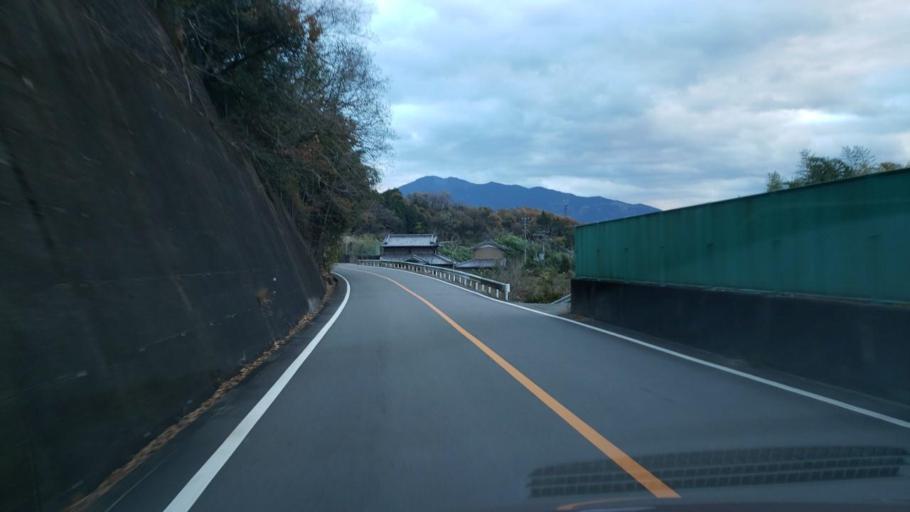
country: JP
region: Tokushima
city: Wakimachi
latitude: 34.0901
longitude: 134.1776
